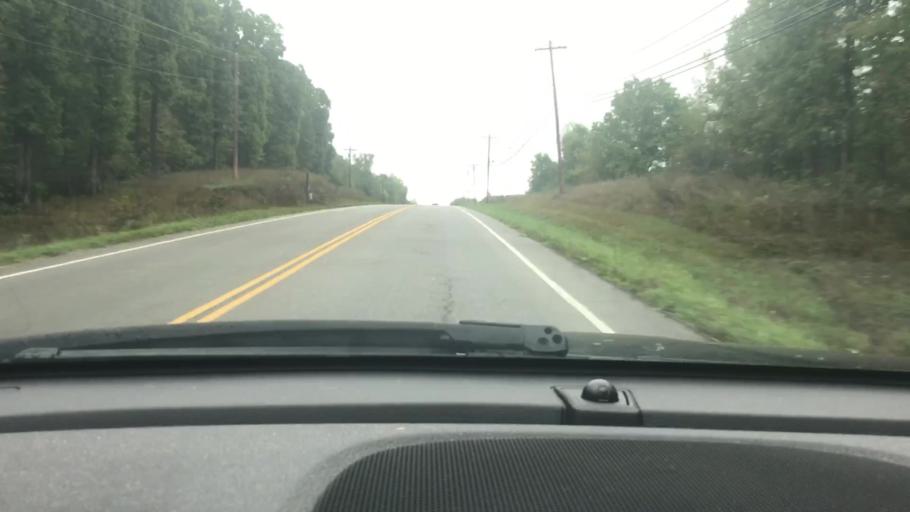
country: US
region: Tennessee
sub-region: Dickson County
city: White Bluff
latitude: 36.1048
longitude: -87.2007
